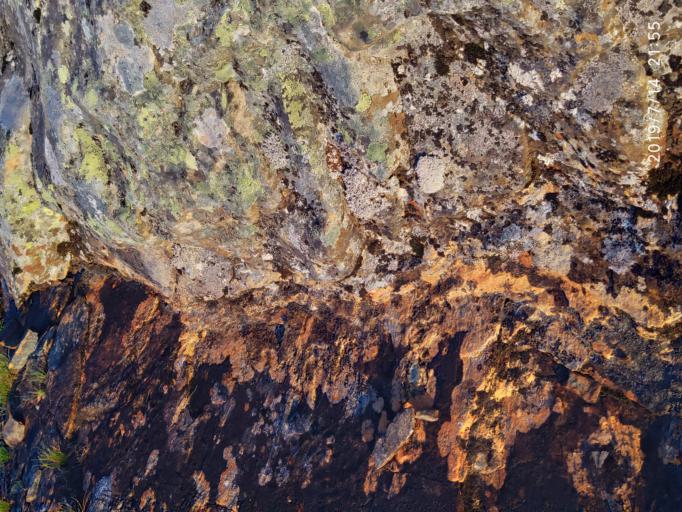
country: NO
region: Hordaland
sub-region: Ullensvang
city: Kinsarvik
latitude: 60.3004
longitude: 6.6952
